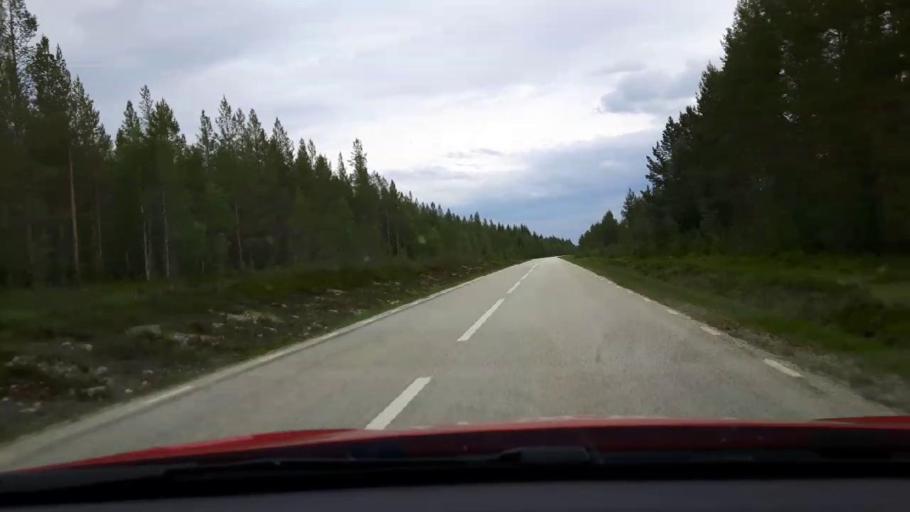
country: SE
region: Jaemtland
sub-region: Bergs Kommun
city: Hoverberg
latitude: 62.7151
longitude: 13.9255
